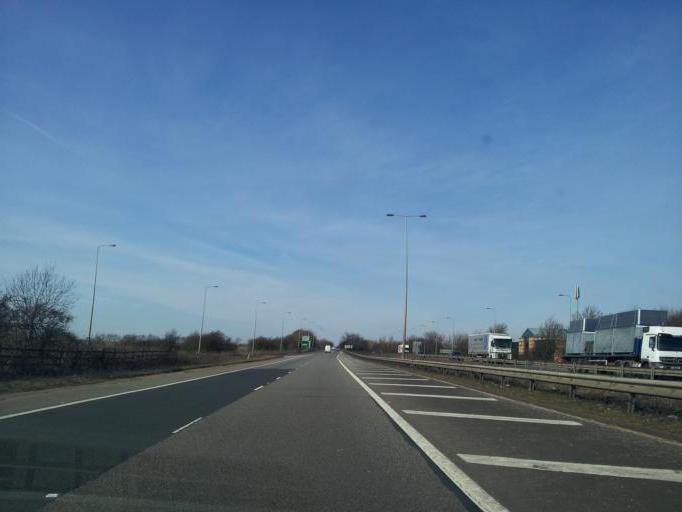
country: GB
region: England
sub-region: Peterborough
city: Castor
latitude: 52.5353
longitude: -0.3207
